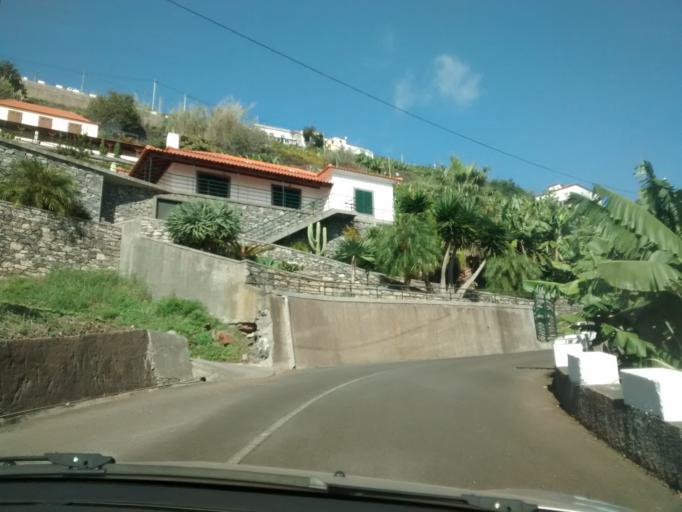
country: PT
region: Madeira
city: Calheta
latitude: 32.7194
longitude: -17.1699
